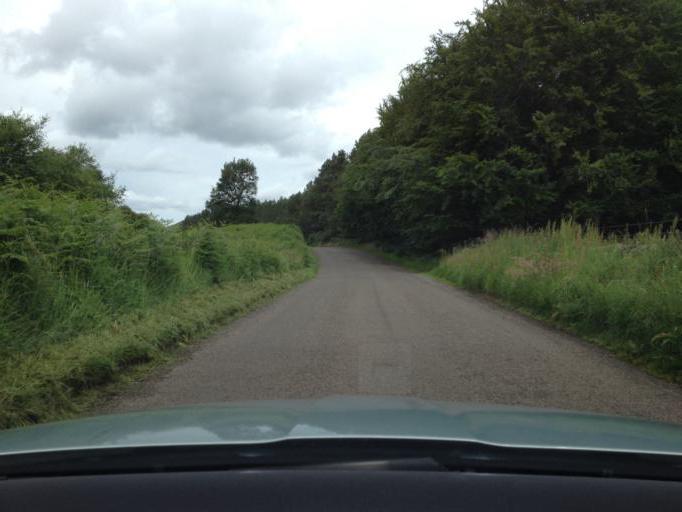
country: GB
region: Scotland
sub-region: Angus
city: Brechin
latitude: 56.8500
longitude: -2.6768
